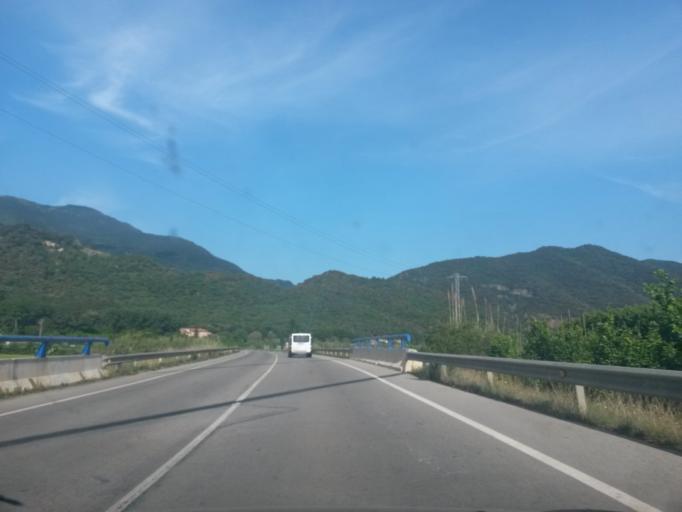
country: ES
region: Catalonia
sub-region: Provincia de Girona
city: la Cellera de Ter
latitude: 41.9788
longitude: 2.6176
